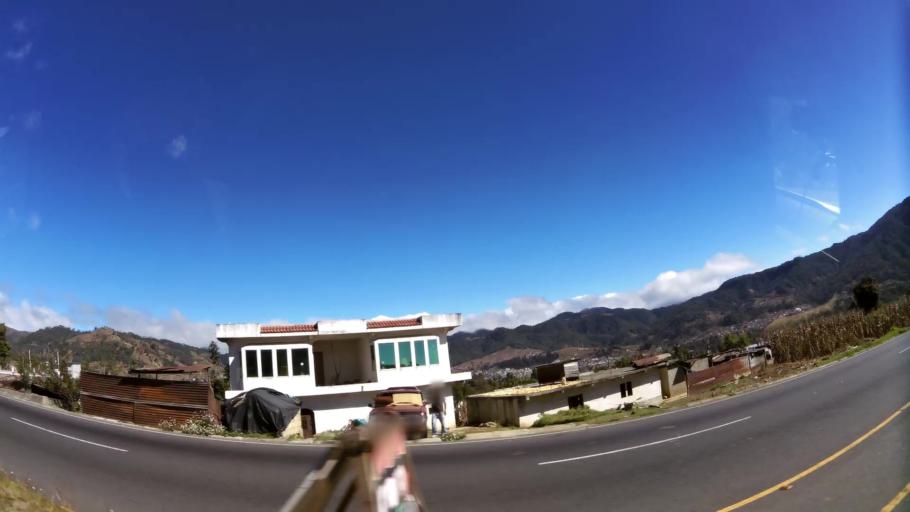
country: GT
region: Solola
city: Nahuala
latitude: 14.8261
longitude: -91.3312
